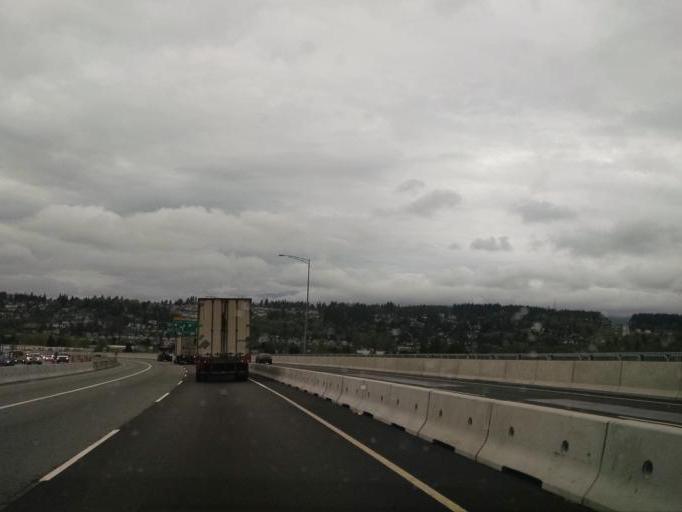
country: CA
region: British Columbia
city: Port Moody
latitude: 49.2243
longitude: -122.8154
